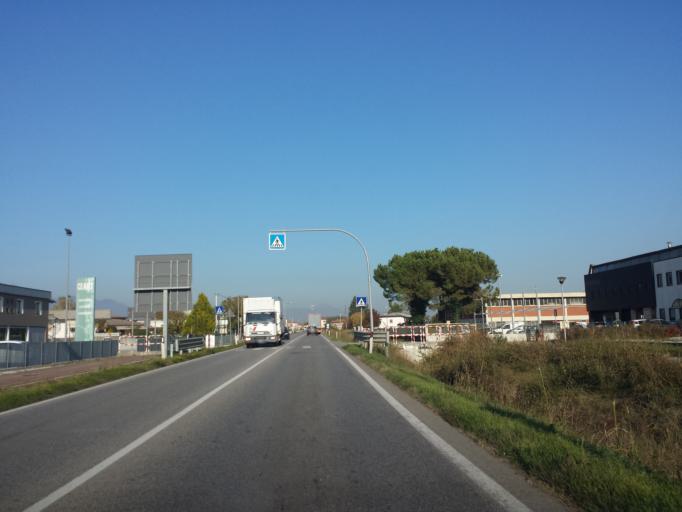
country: IT
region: Veneto
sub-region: Provincia di Treviso
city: Cornuda
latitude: 45.8090
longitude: 12.0086
